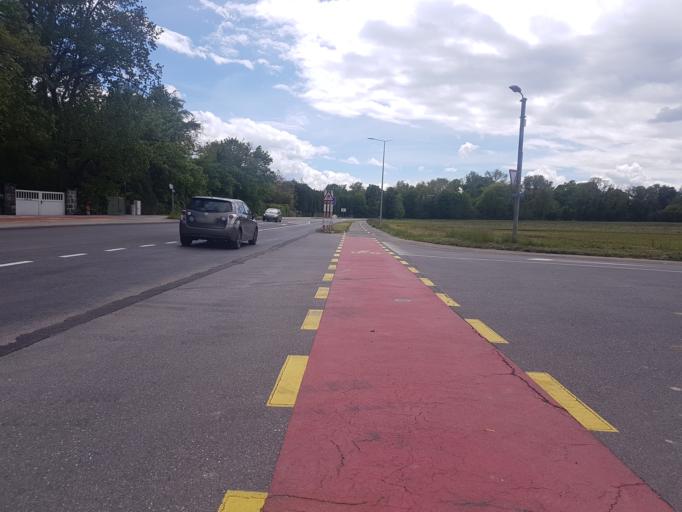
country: CH
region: Vaud
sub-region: Nyon District
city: Founex
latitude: 46.3429
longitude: 6.2055
